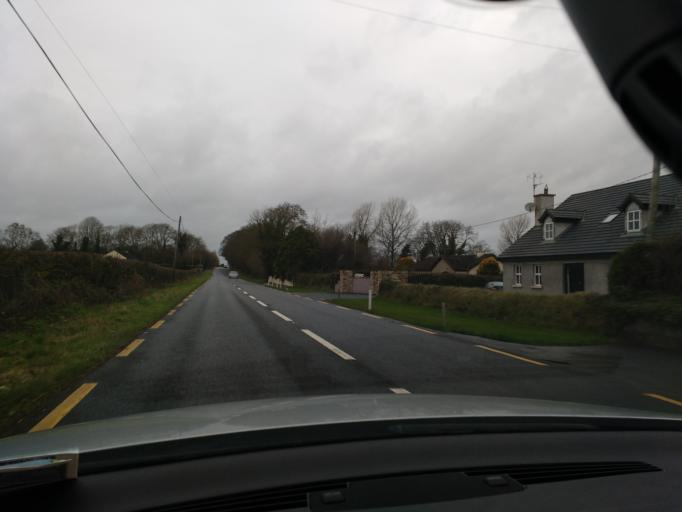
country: IE
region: Munster
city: Thurles
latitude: 52.6726
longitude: -7.7531
